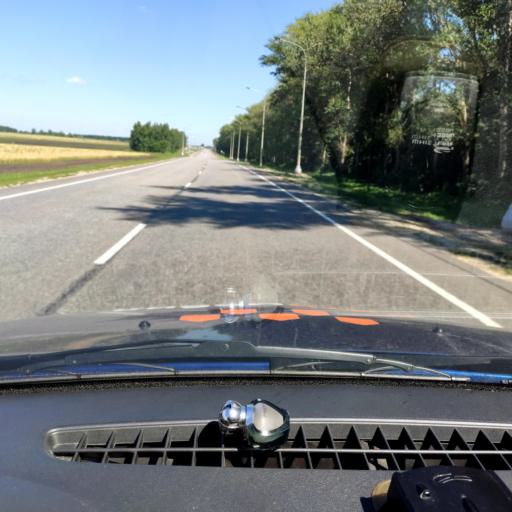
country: RU
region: Orjol
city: Pokrovskoye
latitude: 52.6195
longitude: 36.7458
